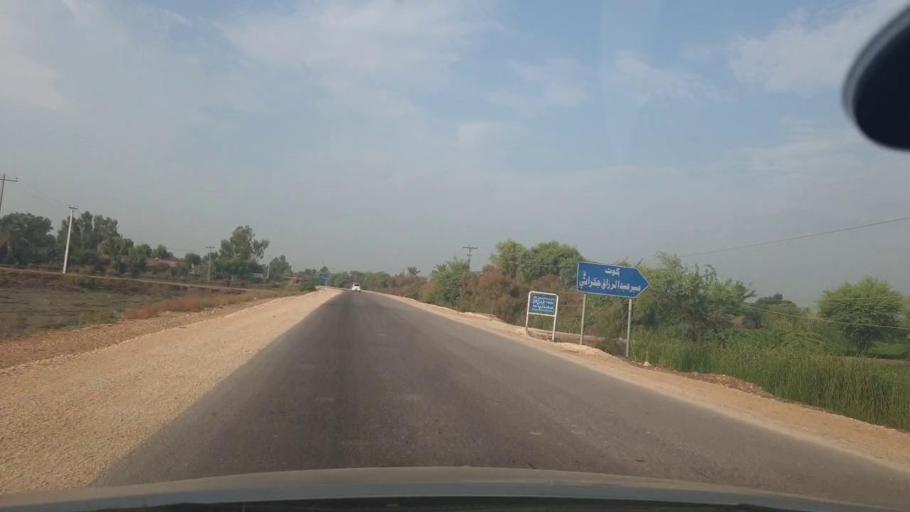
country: PK
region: Sindh
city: Jacobabad
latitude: 28.2175
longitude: 68.3703
